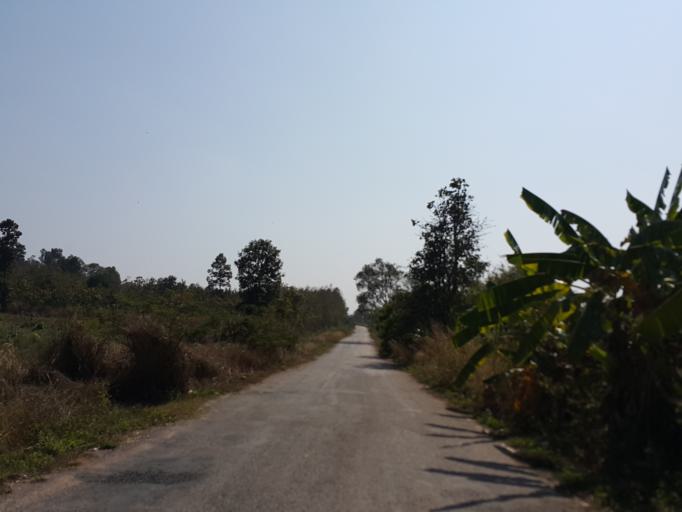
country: TH
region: Lampang
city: Wang Nuea
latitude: 19.0177
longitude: 99.6233
